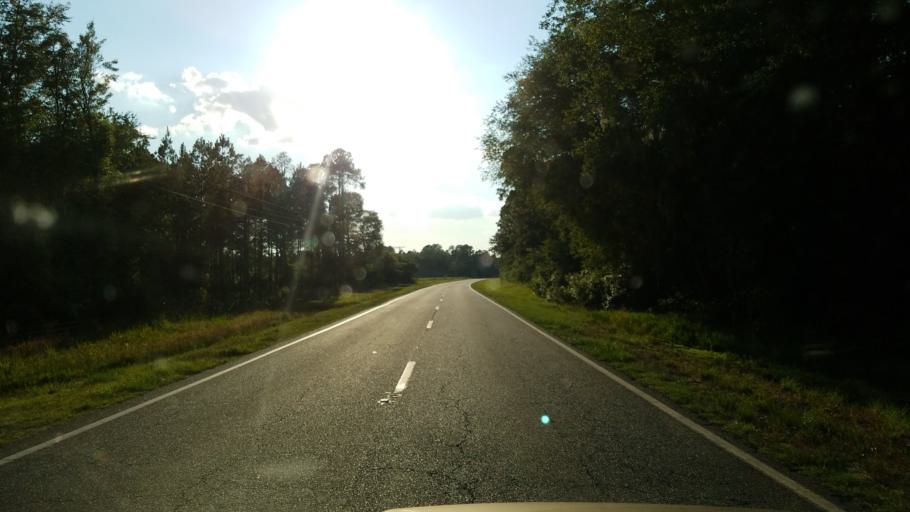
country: US
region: Georgia
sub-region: Berrien County
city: Nashville
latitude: 31.1911
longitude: -83.2067
